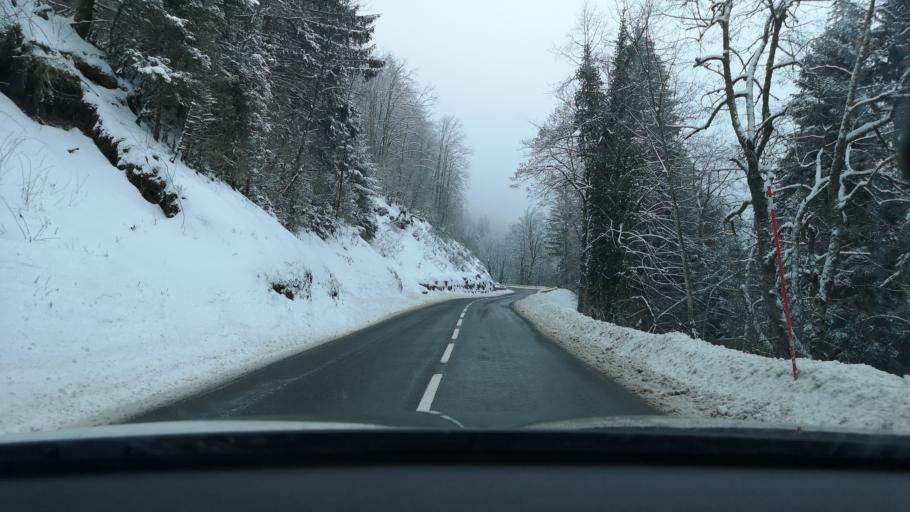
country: FR
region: Rhone-Alpes
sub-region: Departement de l'Ain
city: Arbent
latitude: 46.2530
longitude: 5.7067
